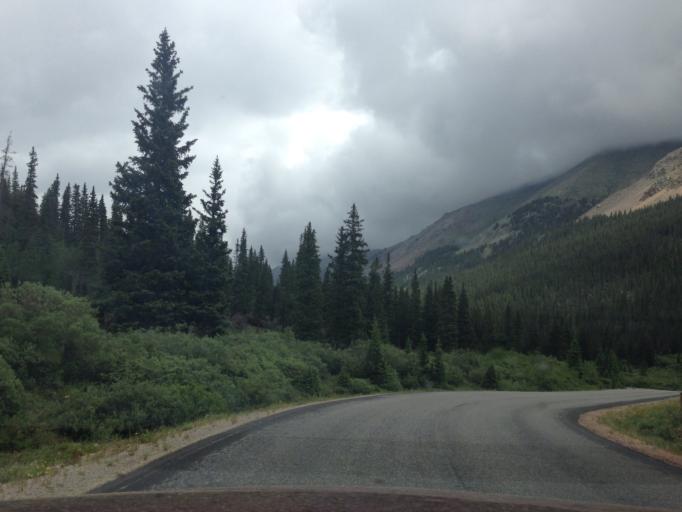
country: US
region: Colorado
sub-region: Clear Creek County
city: Georgetown
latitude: 39.6127
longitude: -105.7180
